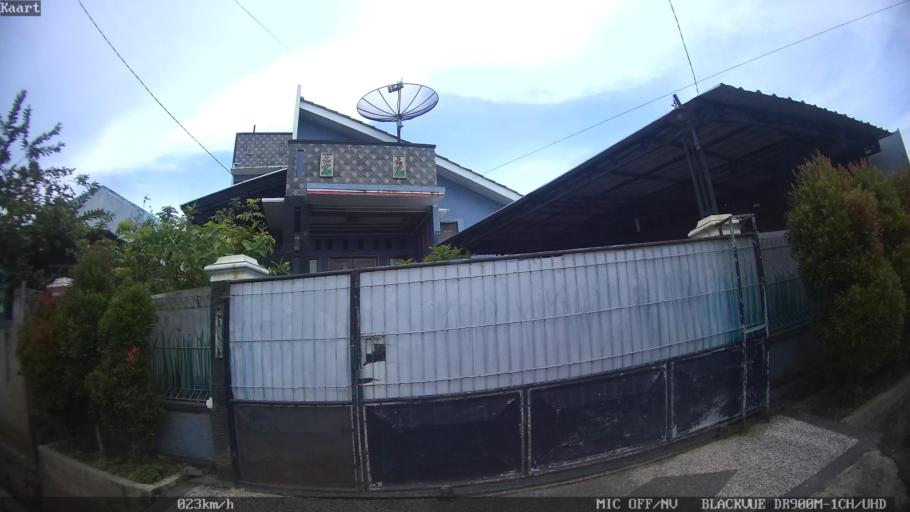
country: ID
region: Lampung
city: Kedaton
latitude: -5.3881
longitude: 105.2021
